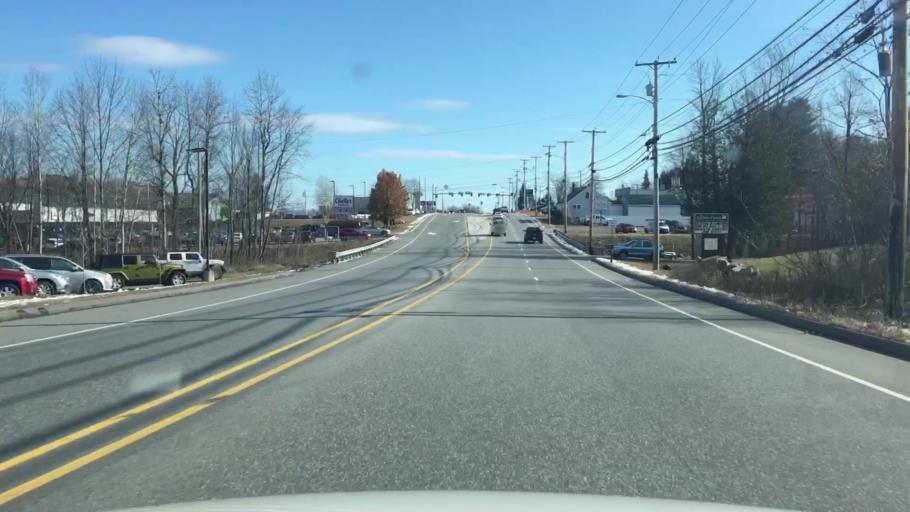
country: US
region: Maine
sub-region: Kennebec County
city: Manchester
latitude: 44.3206
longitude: -69.8269
